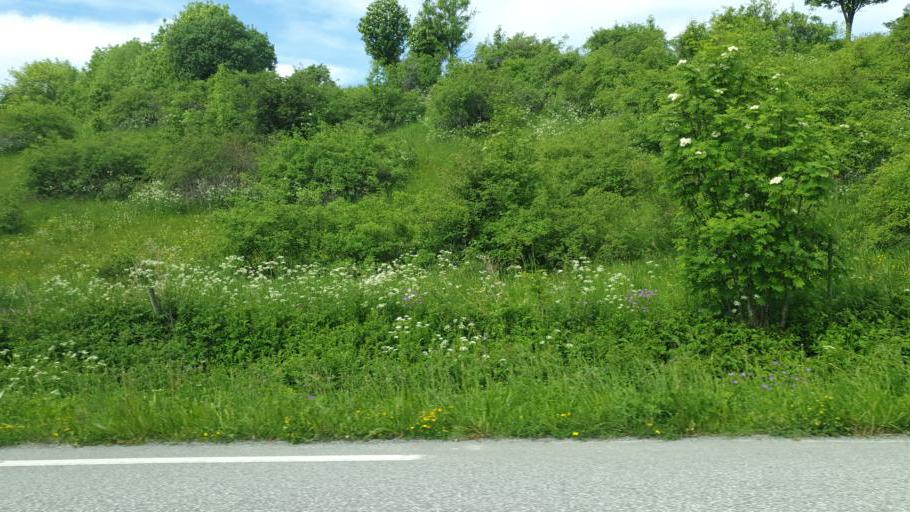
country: NO
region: Sor-Trondelag
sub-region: Trondheim
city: Trondheim
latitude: 63.5858
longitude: 10.4205
